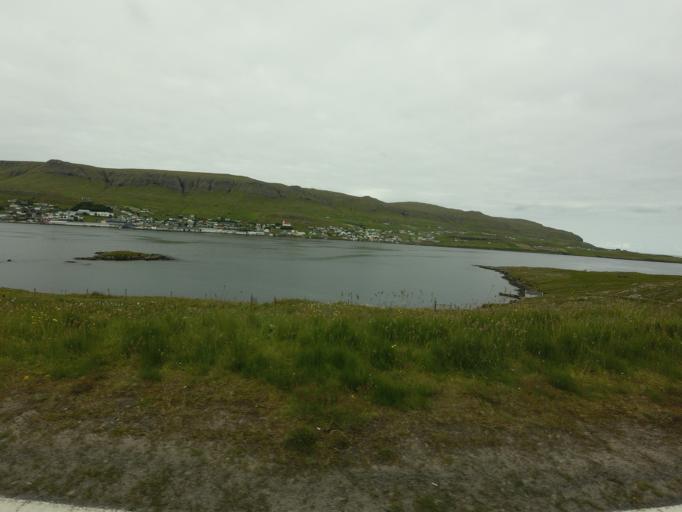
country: FO
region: Suduroy
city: Tvoroyri
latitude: 61.5457
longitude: -6.8141
